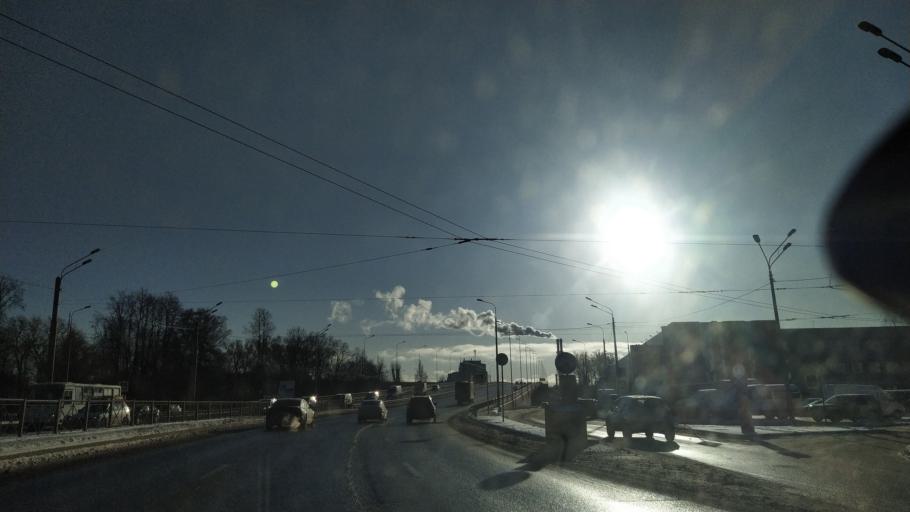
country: RU
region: Leningrad
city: Chernaya Rechka
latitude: 59.9964
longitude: 30.3000
